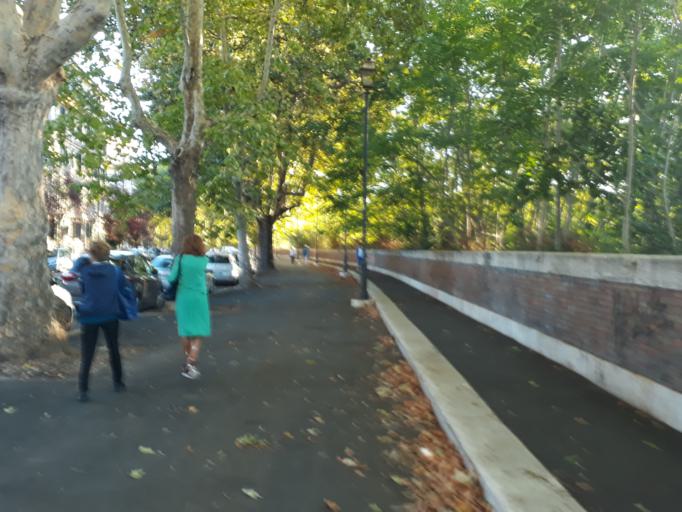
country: VA
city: Vatican City
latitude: 41.8798
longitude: 12.4716
